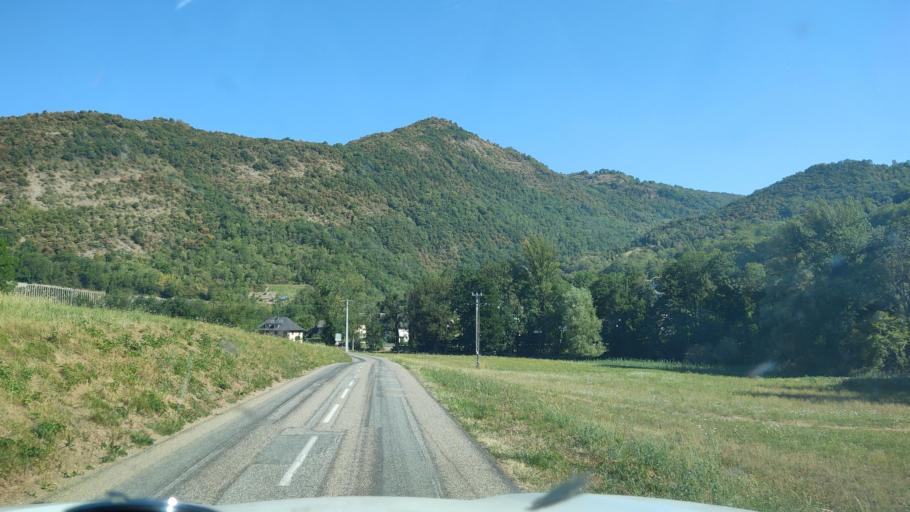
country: FR
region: Rhone-Alpes
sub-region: Departement de la Savoie
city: Challes-les-Eaux
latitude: 45.5379
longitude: 6.0063
